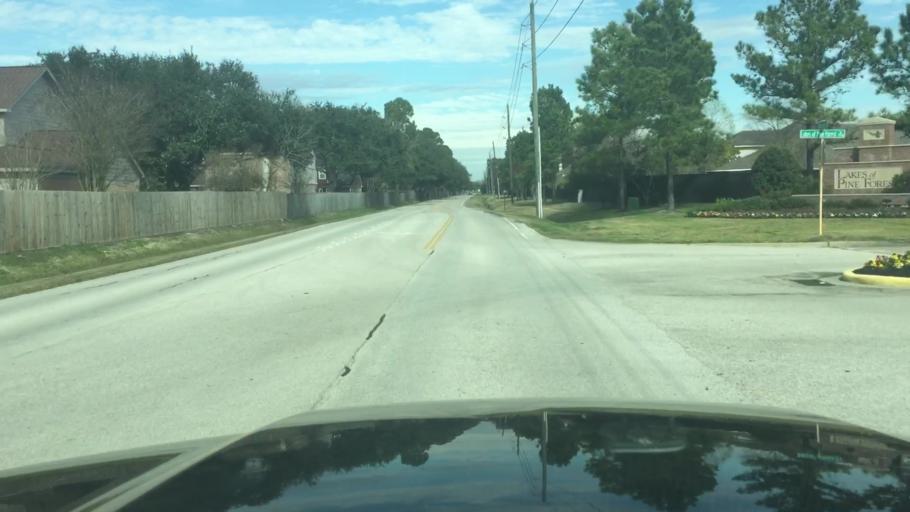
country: US
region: Texas
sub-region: Harris County
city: Oak Cliff Place
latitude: 29.8401
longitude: -95.6751
